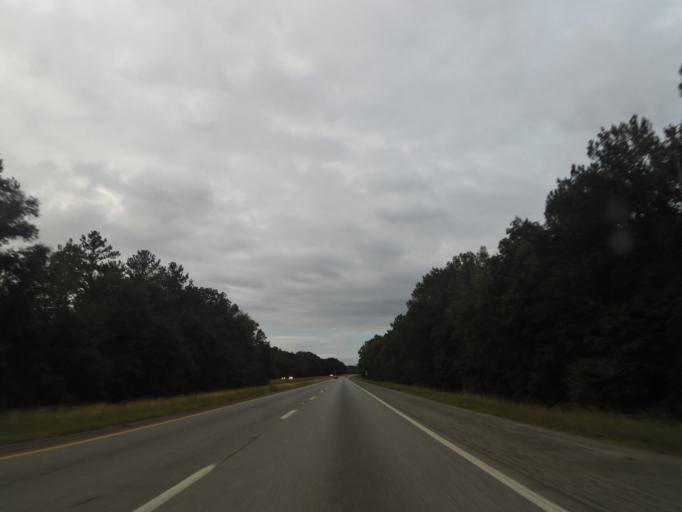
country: US
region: Alabama
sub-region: Saint Clair County
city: Ashville
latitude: 33.8211
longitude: -86.3449
